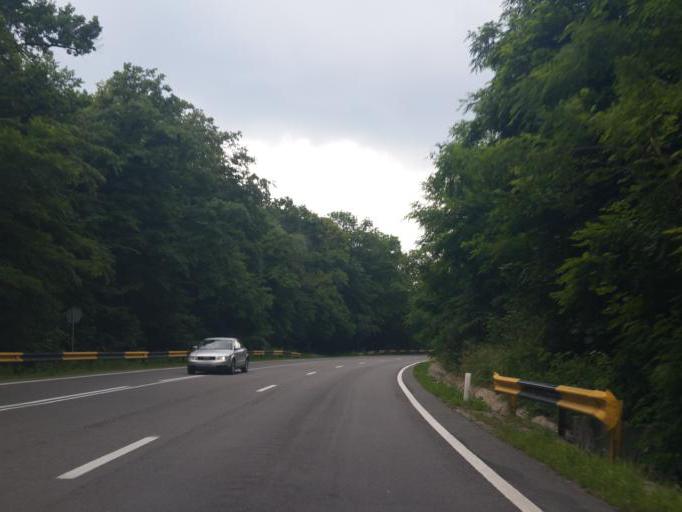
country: RO
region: Salaj
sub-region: Comuna Treznea
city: Treznea
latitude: 47.1459
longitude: 23.1011
